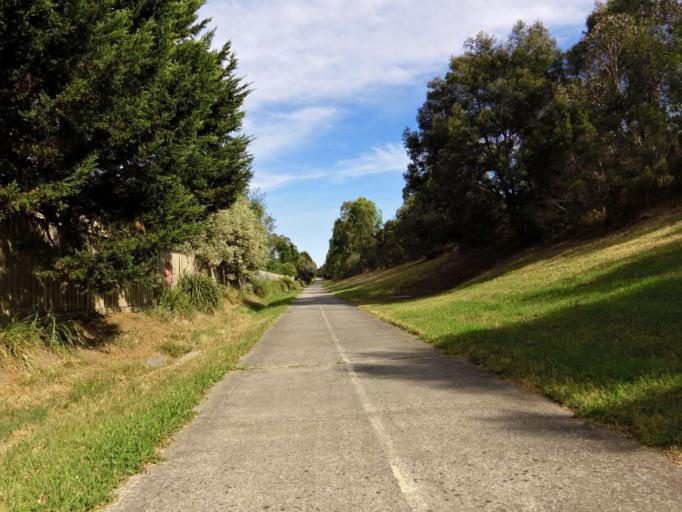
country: AU
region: Victoria
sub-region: Casey
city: Narre Warren
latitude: -38.0241
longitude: 145.3172
